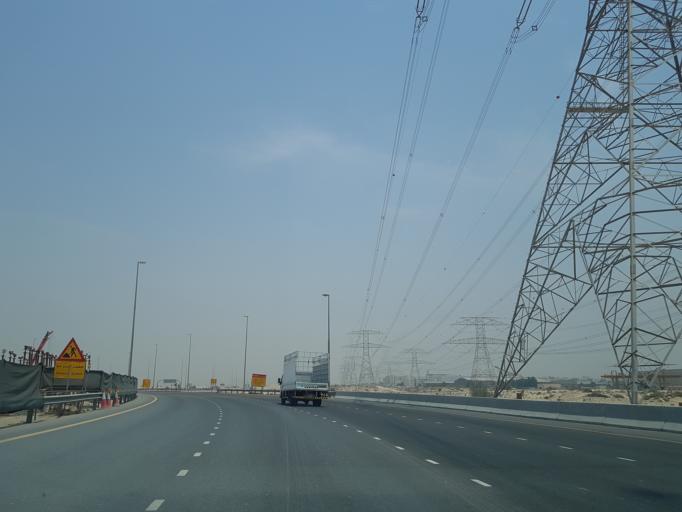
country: AE
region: Dubai
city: Dubai
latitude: 24.9934
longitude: 55.1875
